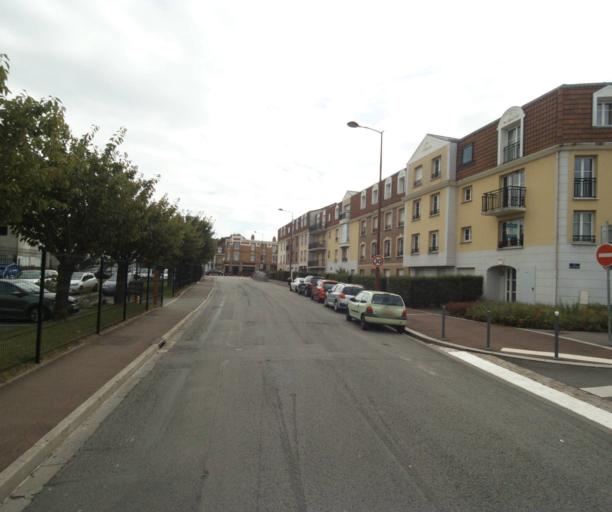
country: FR
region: Nord-Pas-de-Calais
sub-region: Departement du Nord
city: Marcq-en-Baroeul
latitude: 50.6584
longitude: 3.0831
